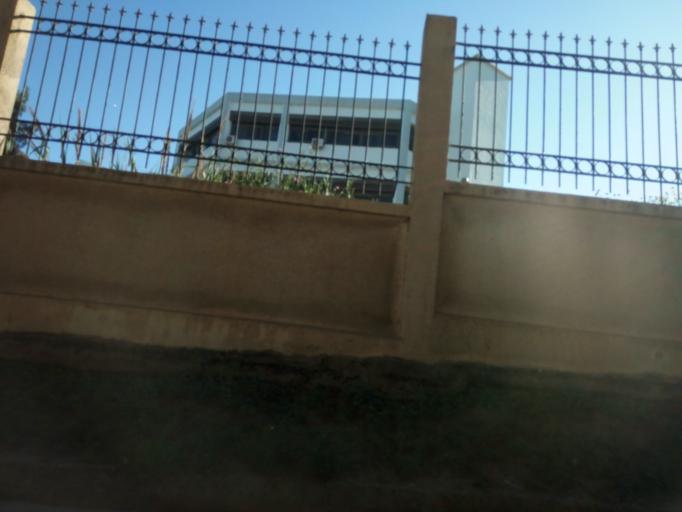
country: DZ
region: Tipaza
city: Saoula
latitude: 36.7274
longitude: 3.0063
